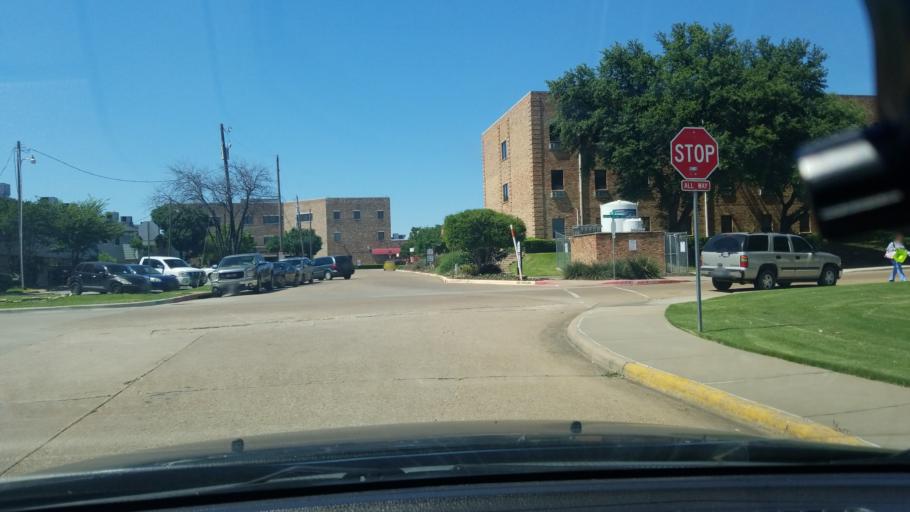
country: US
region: Texas
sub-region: Dallas County
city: Mesquite
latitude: 32.7771
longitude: -96.6009
